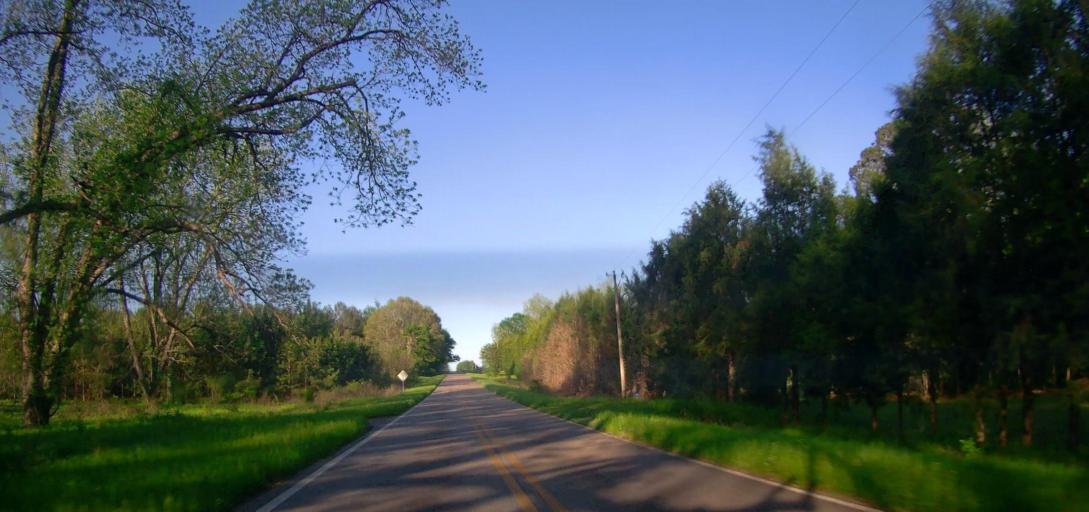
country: US
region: Georgia
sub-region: Macon County
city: Oglethorpe
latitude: 32.3003
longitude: -84.1416
